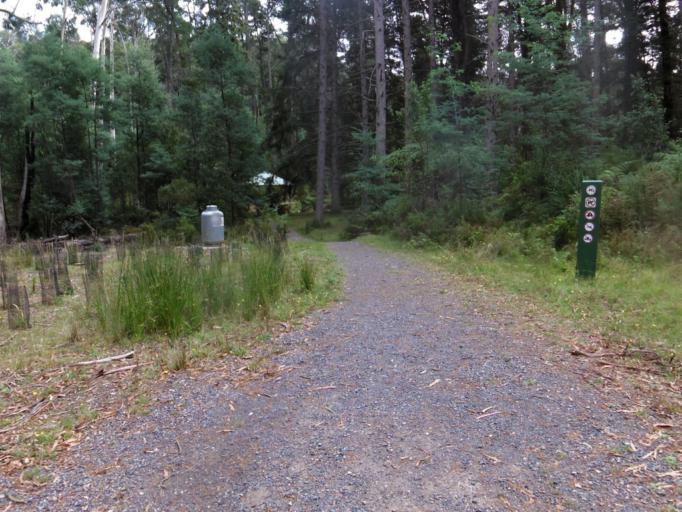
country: AU
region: Victoria
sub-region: Yarra Ranges
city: Healesville
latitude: -37.6281
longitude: 145.5361
